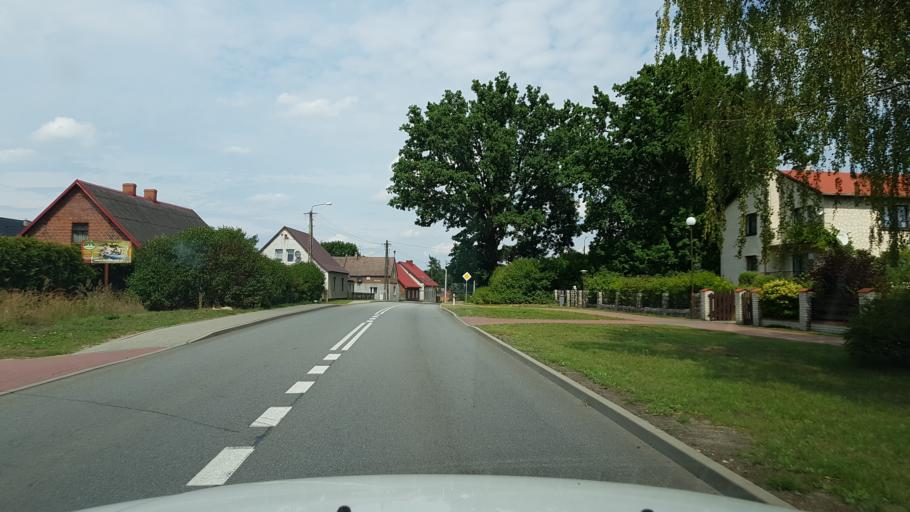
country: PL
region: West Pomeranian Voivodeship
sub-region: Powiat walecki
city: Walcz
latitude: 53.2991
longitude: 16.5283
